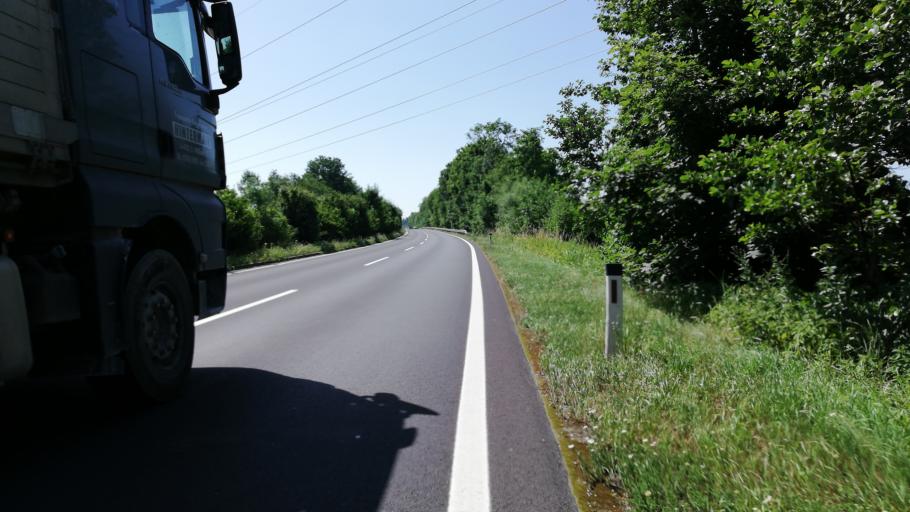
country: AT
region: Upper Austria
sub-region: Wels Stadt
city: Wels
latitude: 48.1898
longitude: 14.0145
